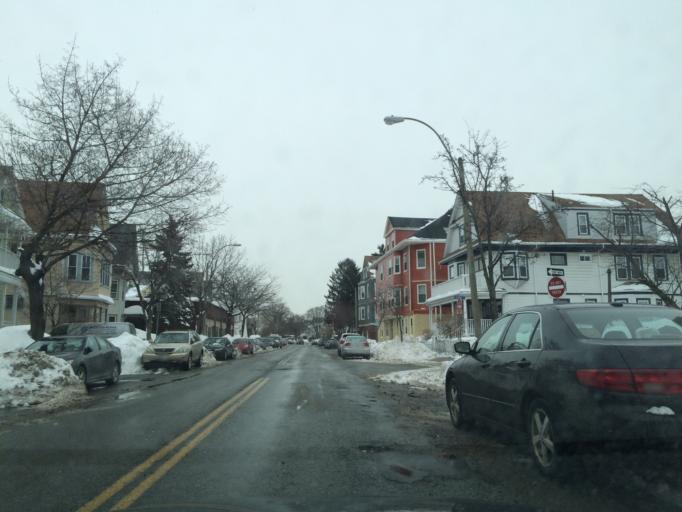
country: US
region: Massachusetts
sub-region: Middlesex County
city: Somerville
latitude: 42.3900
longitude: -71.1076
